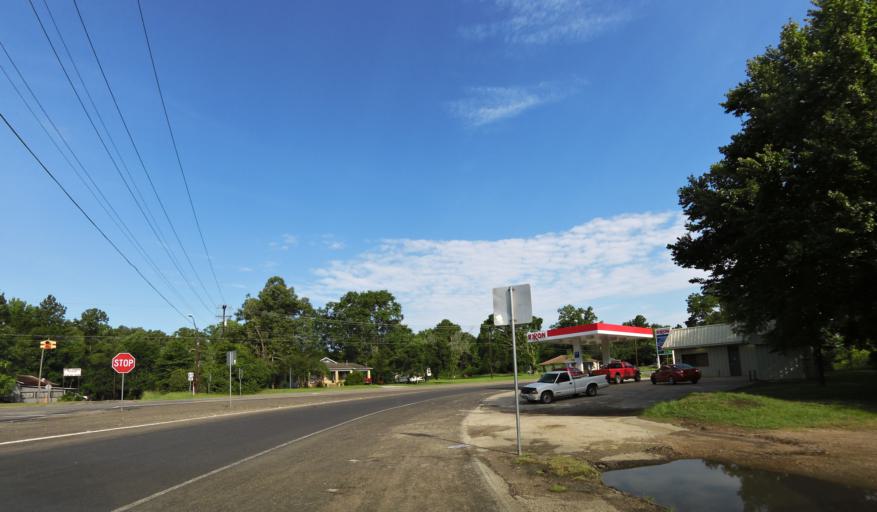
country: US
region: Texas
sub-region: Angelina County
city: Huntington
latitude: 31.1586
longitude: -94.4281
